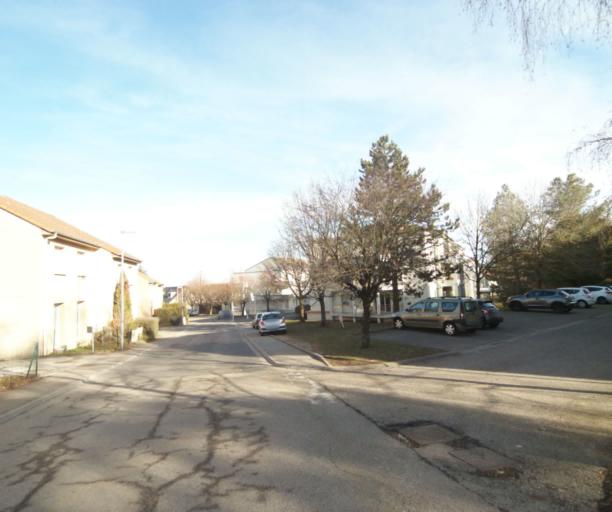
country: FR
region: Lorraine
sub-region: Departement de Meurthe-et-Moselle
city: Villers-les-Nancy
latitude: 48.6495
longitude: 6.1562
